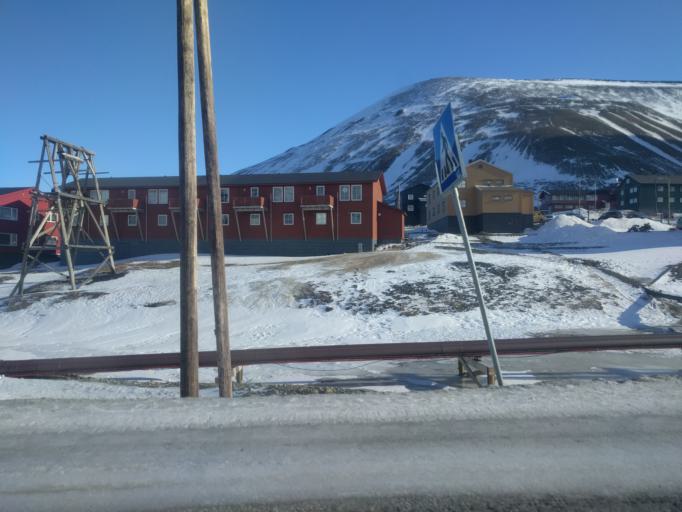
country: SJ
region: Svalbard
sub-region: Spitsbergen
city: Longyearbyen
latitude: 78.2125
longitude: 15.6161
